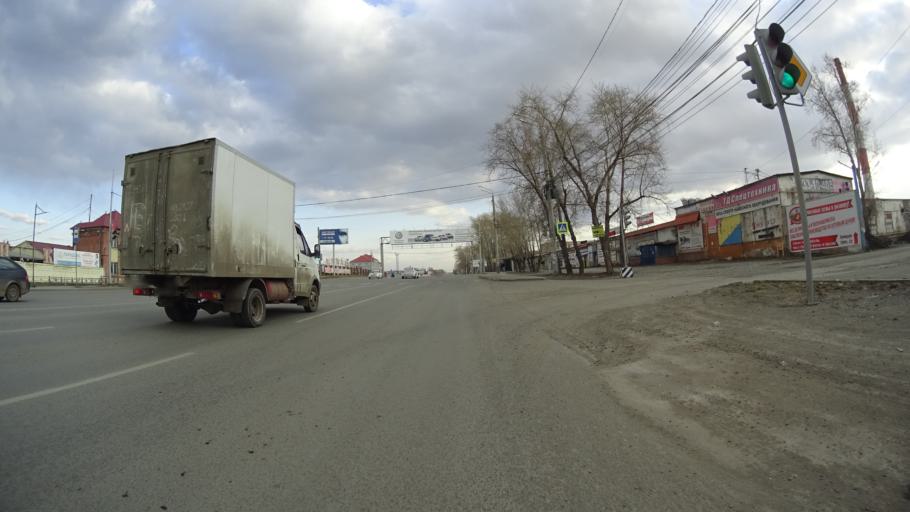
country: RU
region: Chelyabinsk
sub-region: Gorod Chelyabinsk
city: Chelyabinsk
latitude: 55.1112
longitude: 61.3867
